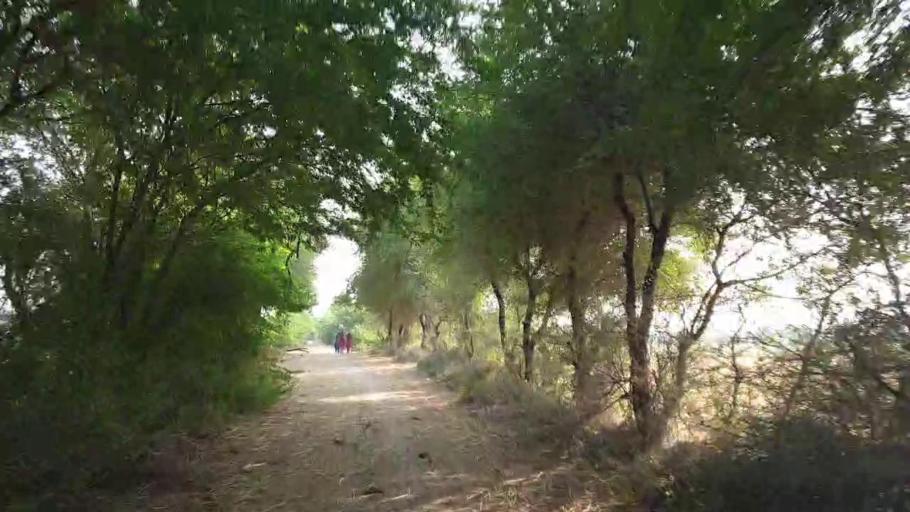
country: PK
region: Sindh
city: Kario
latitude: 24.8990
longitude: 68.5673
